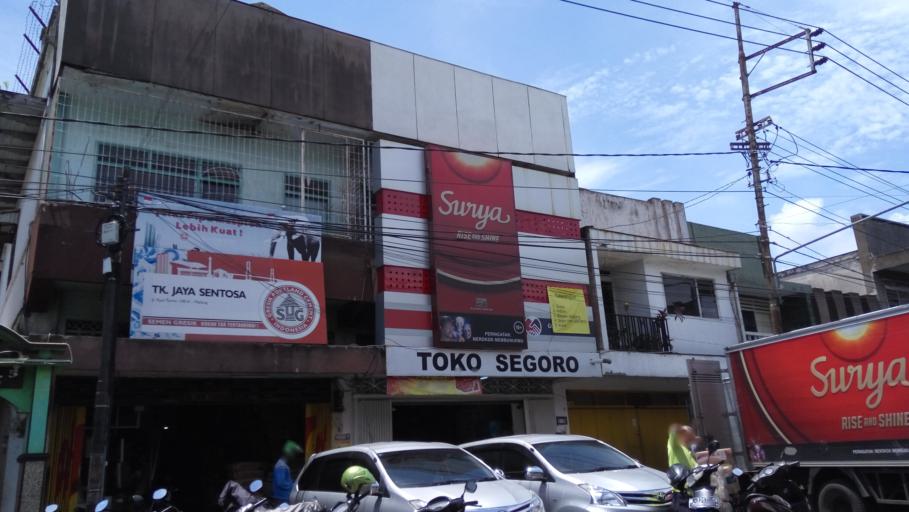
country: ID
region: East Java
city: Malang
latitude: -7.9889
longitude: 112.6340
